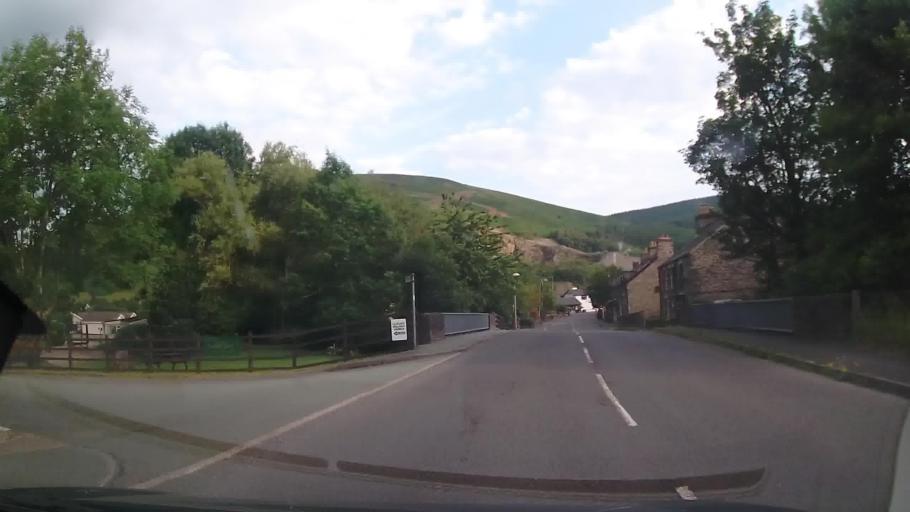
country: GB
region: Wales
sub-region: Sir Powys
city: Llangynog
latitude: 52.8254
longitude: -3.4065
